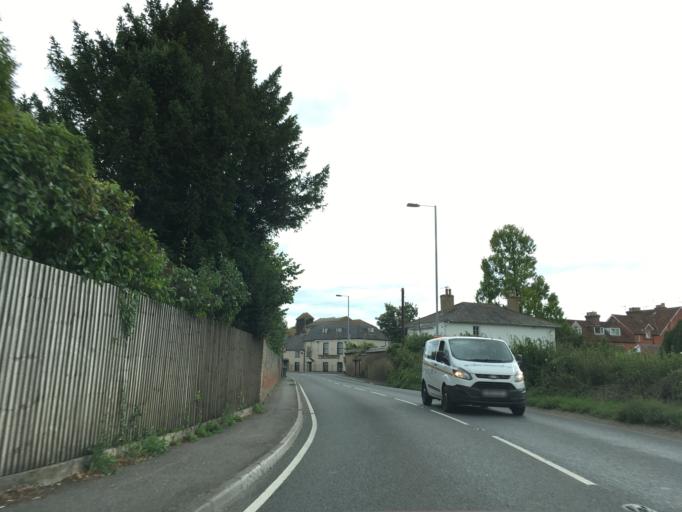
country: GB
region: England
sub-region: Wiltshire
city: Wilton
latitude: 51.0839
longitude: -1.8601
